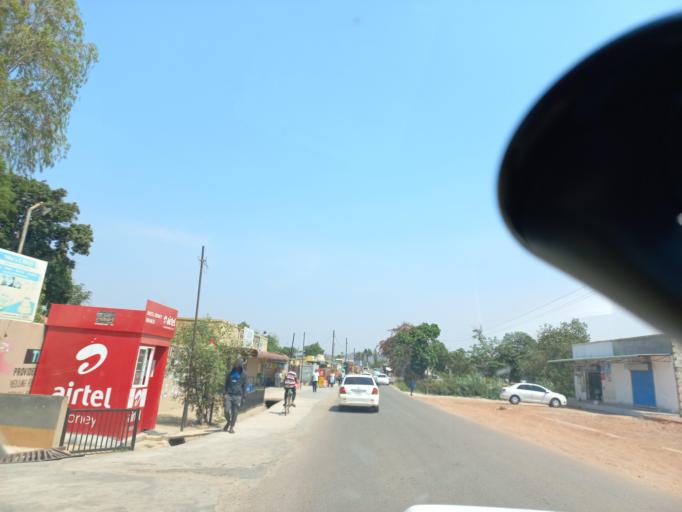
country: ZM
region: Lusaka
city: Kafue
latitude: -15.7462
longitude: 28.1788
